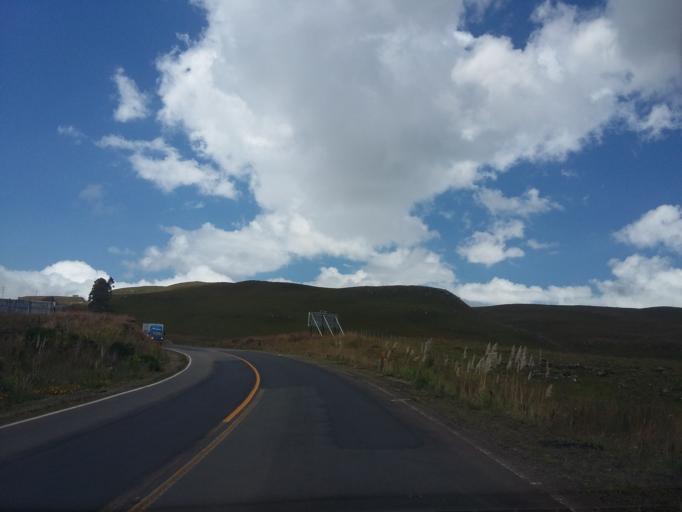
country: BR
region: Santa Catarina
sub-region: Lauro Muller
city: Lauro Muller
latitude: -28.3610
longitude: -49.5895
